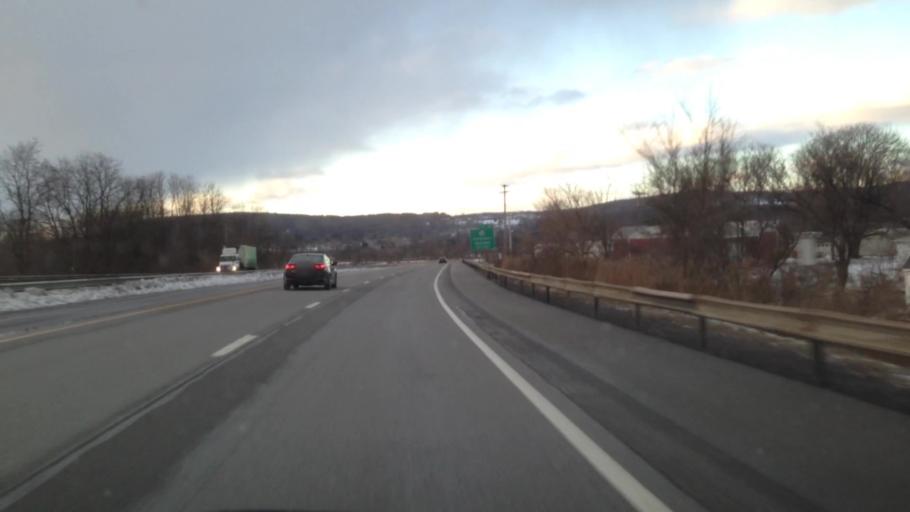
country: US
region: New York
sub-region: Herkimer County
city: Herkimer
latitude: 43.0153
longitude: -74.9777
